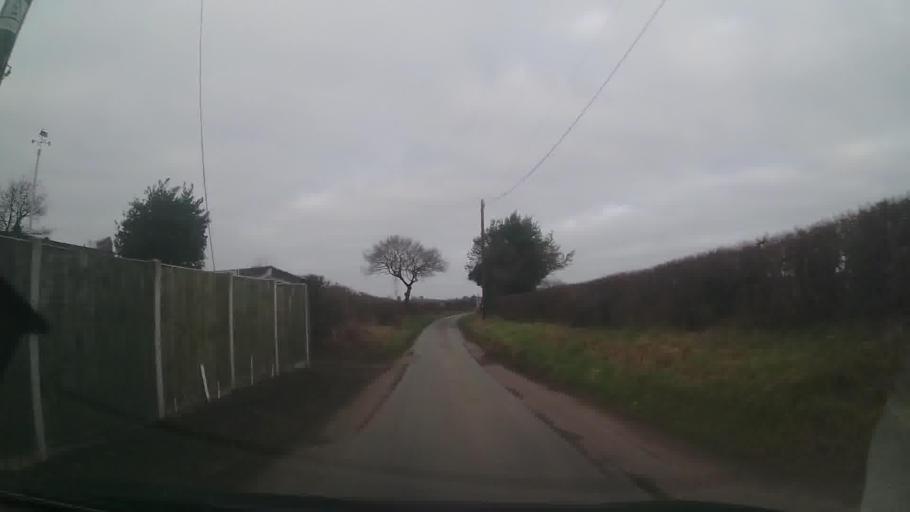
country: GB
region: England
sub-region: Shropshire
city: Petton
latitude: 52.7951
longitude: -2.8409
